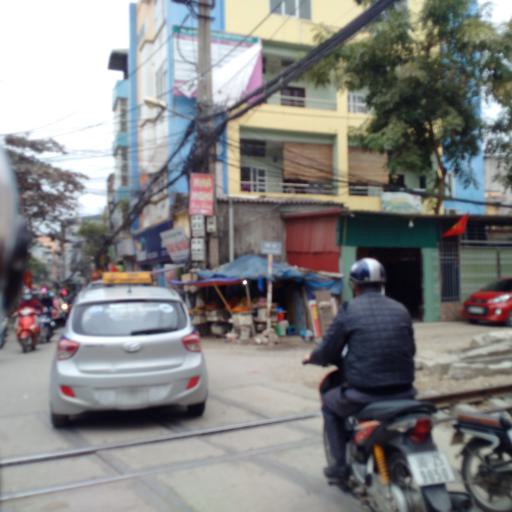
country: VN
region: Ha Noi
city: Cau Dien
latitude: 21.0606
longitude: 105.7817
